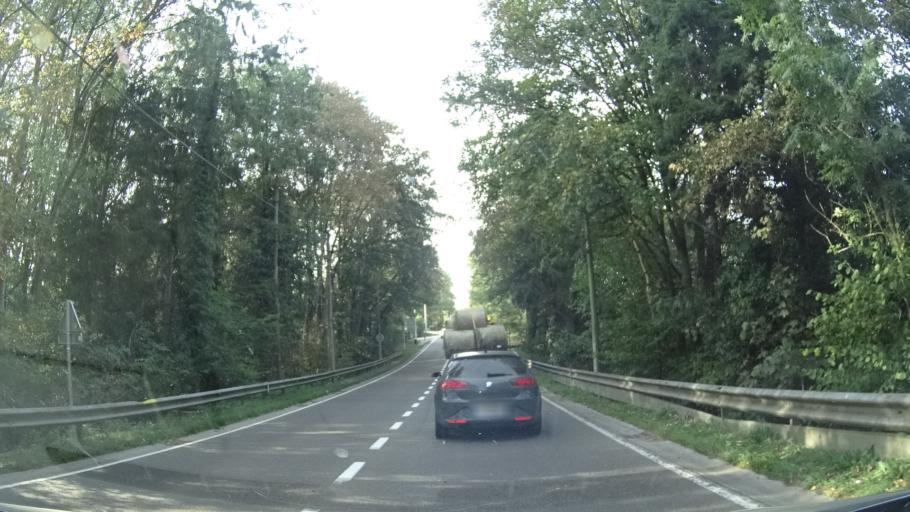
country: BE
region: Wallonia
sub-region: Province du Hainaut
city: Beaumont
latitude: 50.2398
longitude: 4.2371
